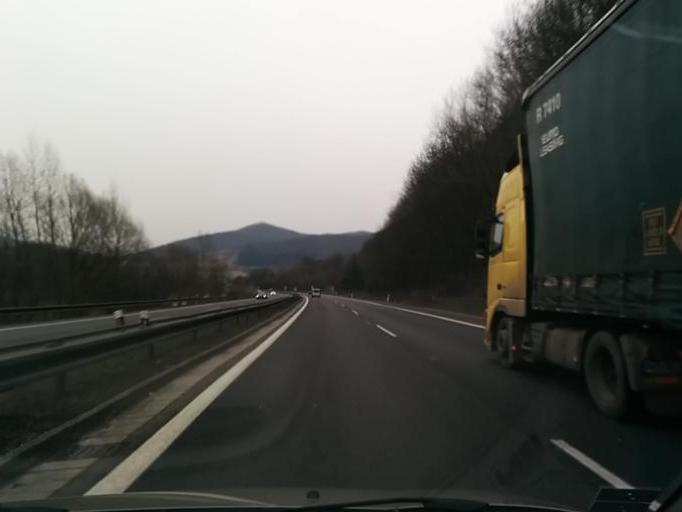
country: SK
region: Banskobystricky
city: Ziar nad Hronom
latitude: 48.5838
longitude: 18.9295
